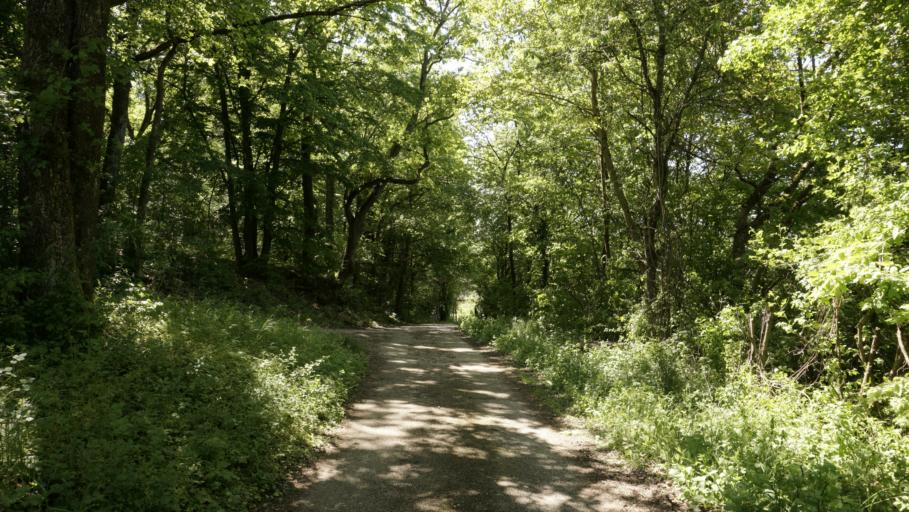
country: DE
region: Baden-Wuerttemberg
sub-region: Karlsruhe Region
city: Mosbach
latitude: 49.3753
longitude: 9.1778
